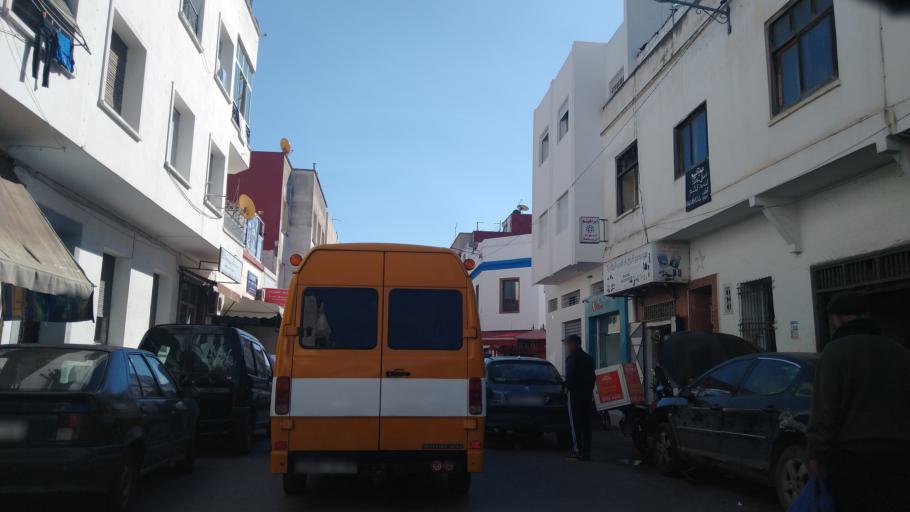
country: MA
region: Rabat-Sale-Zemmour-Zaer
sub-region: Rabat
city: Rabat
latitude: 34.0343
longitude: -6.8210
